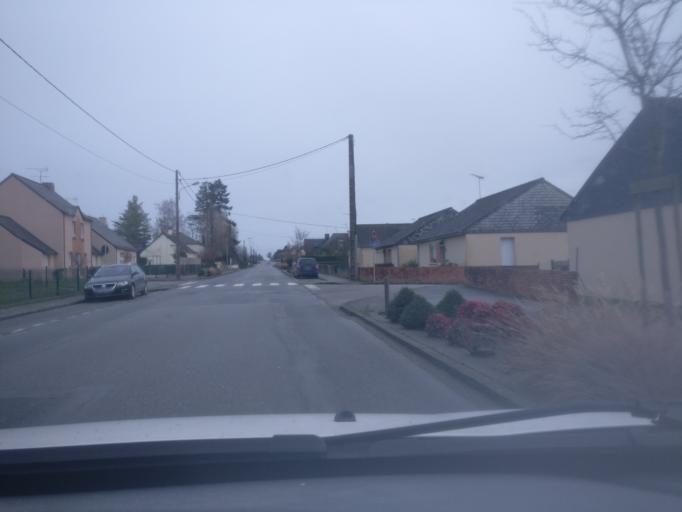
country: FR
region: Brittany
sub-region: Departement d'Ille-et-Vilaine
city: Louvigne-de-Bais
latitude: 48.0512
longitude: -1.3252
